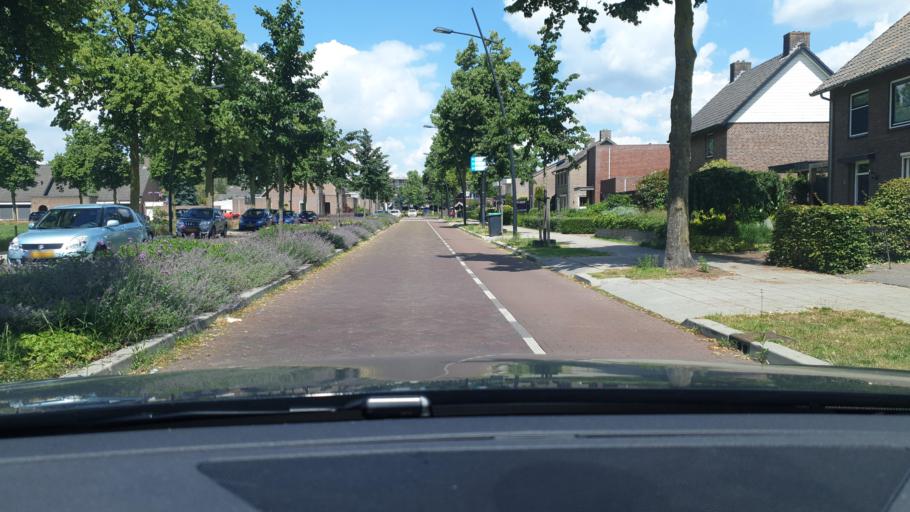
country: NL
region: North Brabant
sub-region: Gemeente Uden
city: Uden
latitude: 51.6556
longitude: 5.6100
